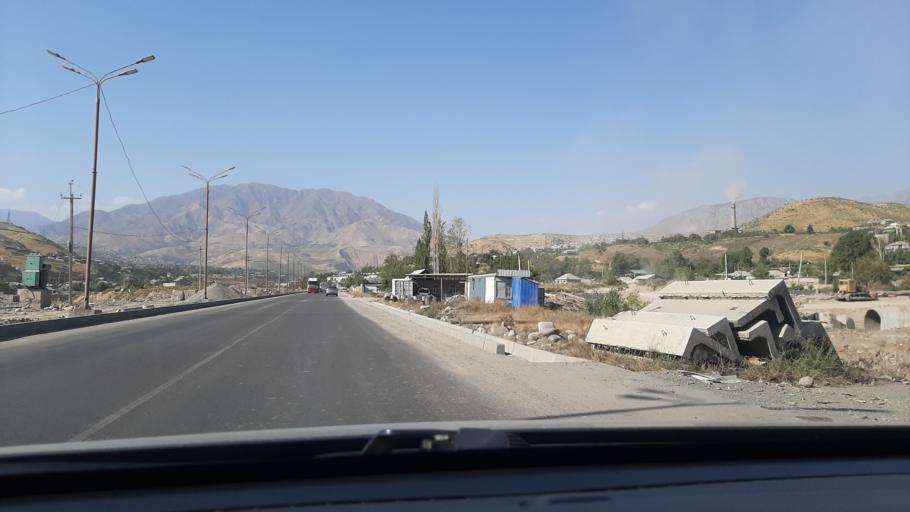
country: TJ
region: Dushanbe
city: Dushanbe
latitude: 38.6363
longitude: 68.7663
